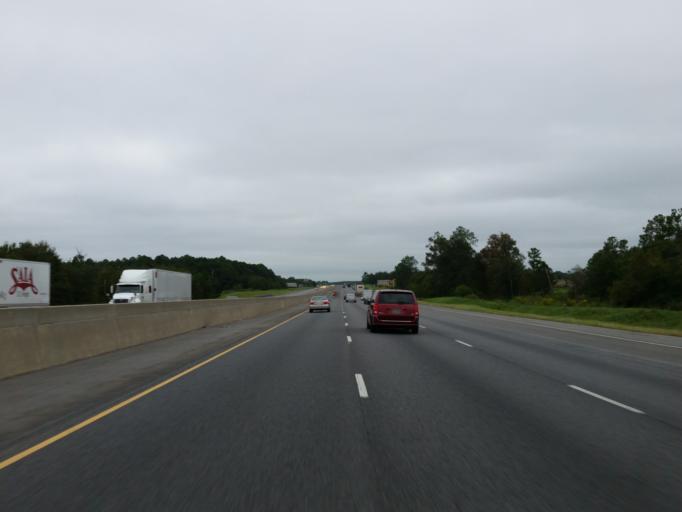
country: US
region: Georgia
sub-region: Turner County
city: Ashburn
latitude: 31.8322
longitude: -83.7131
